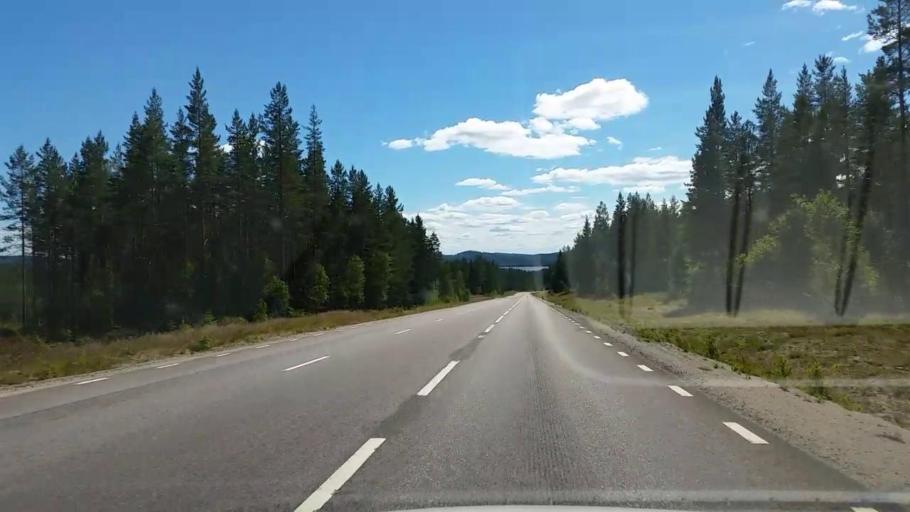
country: SE
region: Gaevleborg
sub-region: Bollnas Kommun
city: Vittsjo
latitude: 61.0564
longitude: 15.8028
